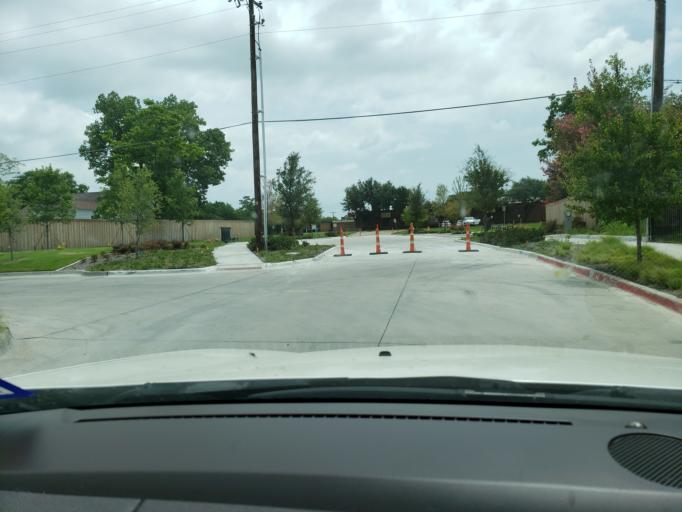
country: US
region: Texas
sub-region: Dallas County
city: Rowlett
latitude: 32.9014
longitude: -96.5638
